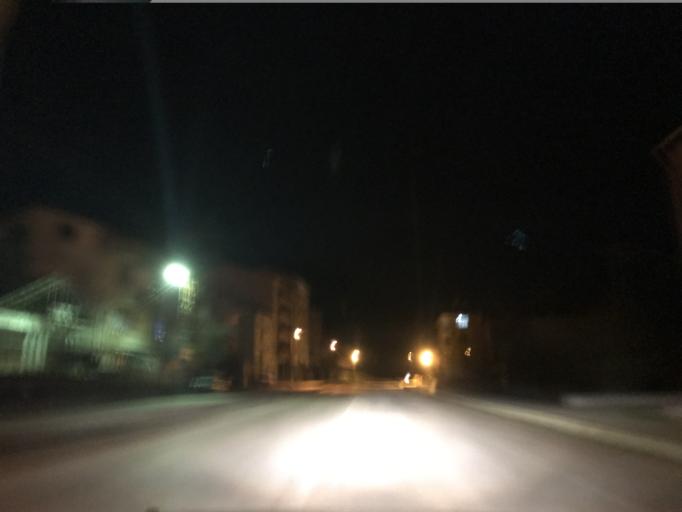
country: TR
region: Kastamonu
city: Igdir
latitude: 41.2251
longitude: 33.1307
